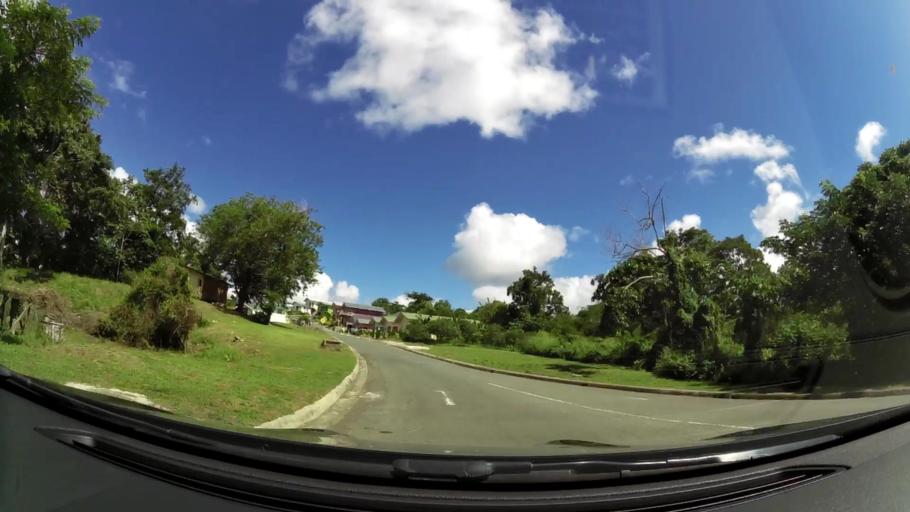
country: TT
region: Tobago
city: Scarborough
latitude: 11.2178
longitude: -60.7719
